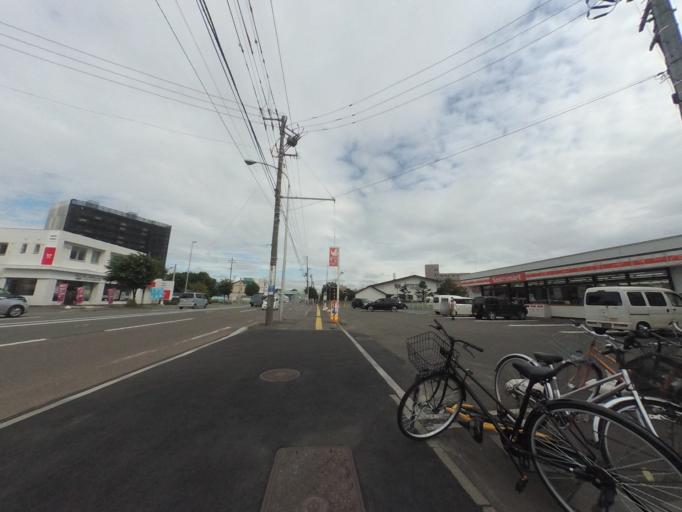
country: JP
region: Hokkaido
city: Sapporo
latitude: 43.0625
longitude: 141.3840
